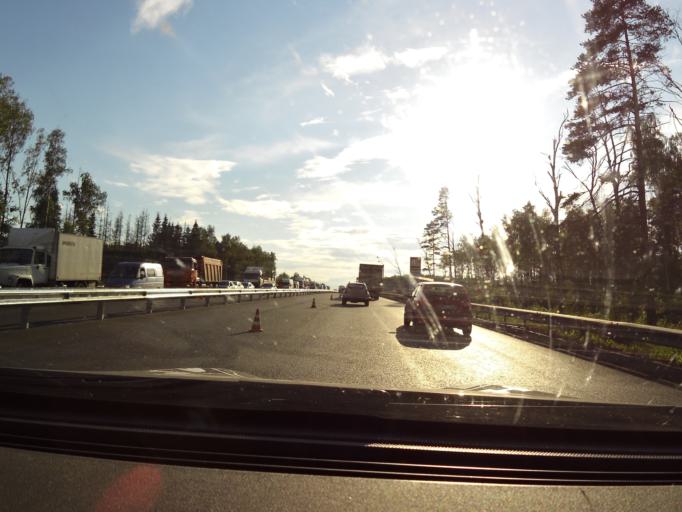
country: RU
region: Vladimir
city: Melekhovo
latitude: 56.2114
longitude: 41.3078
